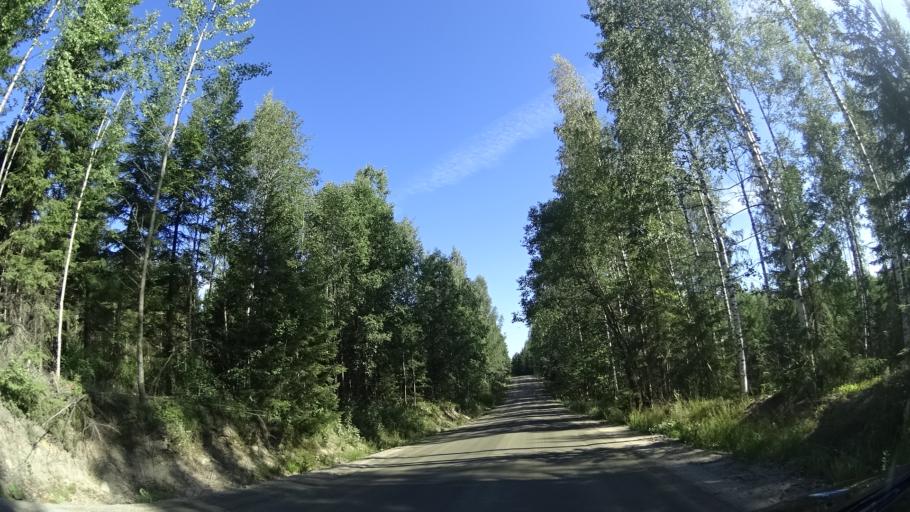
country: FI
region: Central Finland
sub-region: Jyvaeskylae
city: Petaejaevesi
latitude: 62.3236
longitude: 25.3478
